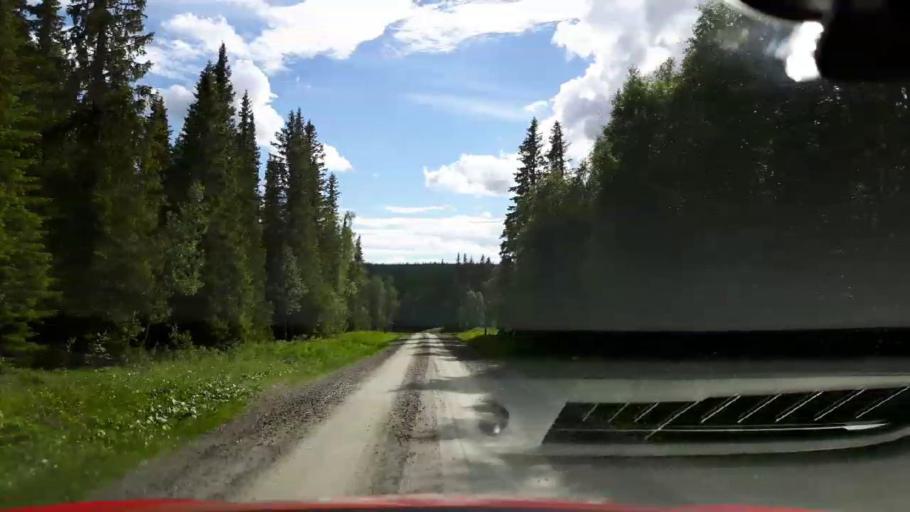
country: SE
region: Jaemtland
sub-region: Krokoms Kommun
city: Valla
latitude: 63.8370
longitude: 14.0431
